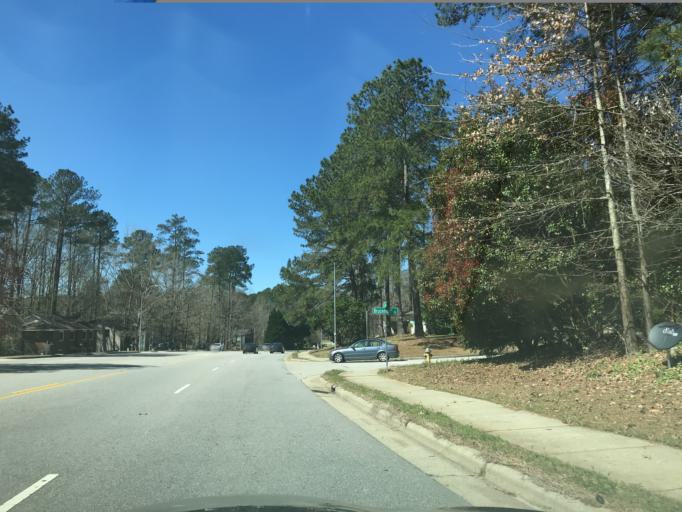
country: US
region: North Carolina
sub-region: Wake County
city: Garner
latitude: 35.6856
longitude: -78.6215
